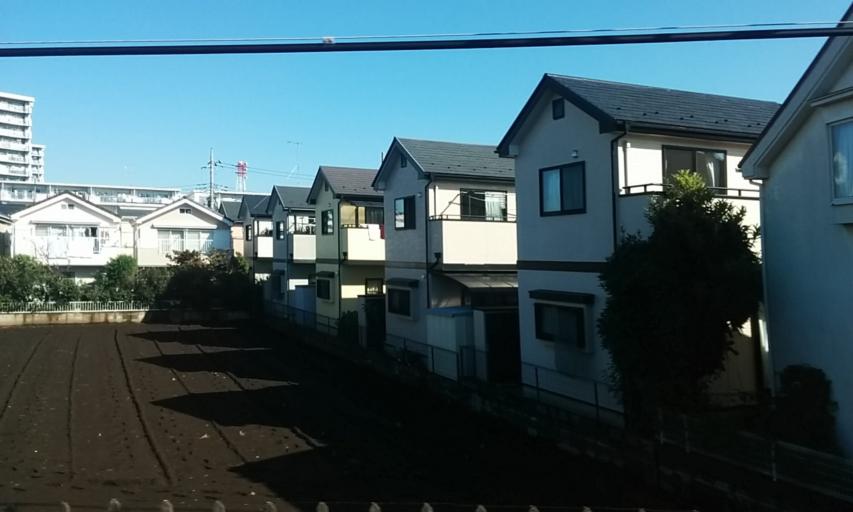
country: JP
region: Tokyo
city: Tanashicho
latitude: 35.7329
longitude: 139.4978
